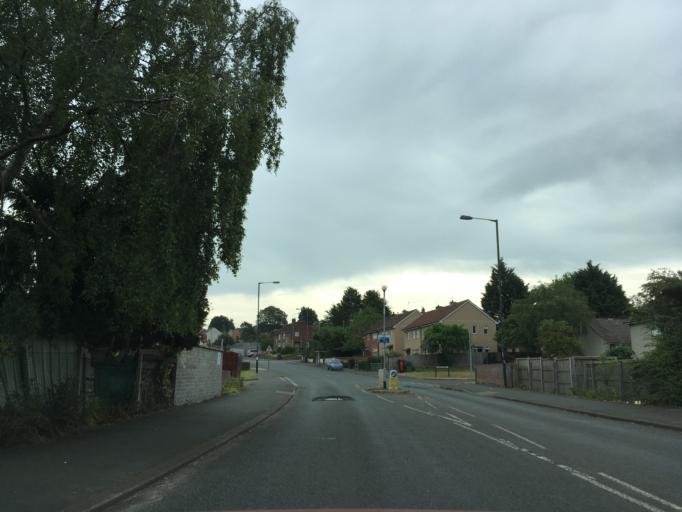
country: GB
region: England
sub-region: South Gloucestershire
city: Stoke Gifford
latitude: 51.4893
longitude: -2.5708
